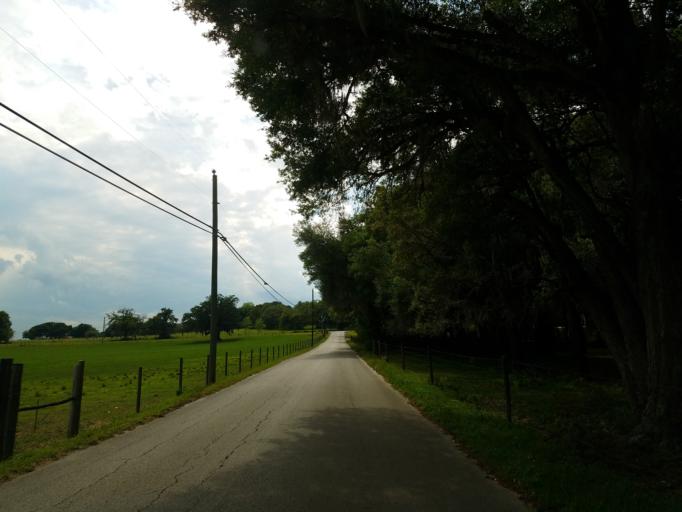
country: US
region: Florida
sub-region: Hernando County
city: Hill 'n Dale
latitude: 28.5426
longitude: -82.2984
